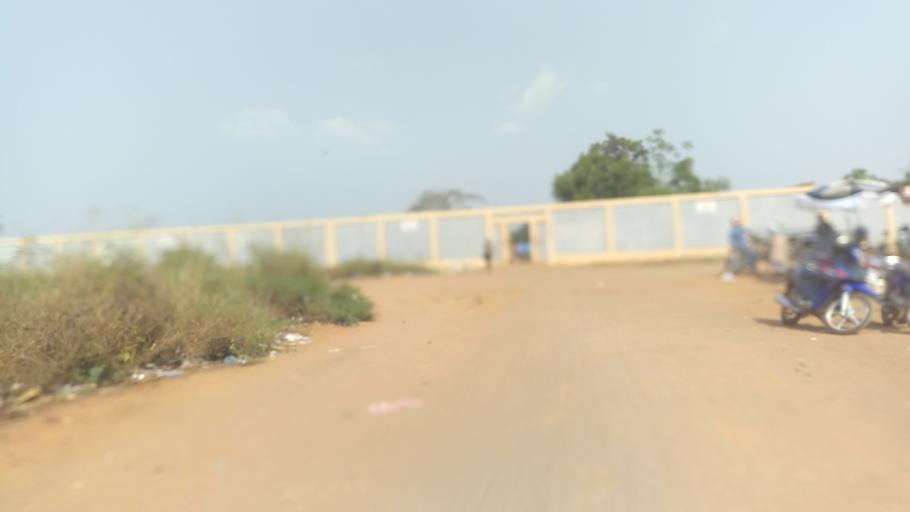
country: TG
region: Maritime
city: Lome
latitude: 6.1701
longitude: 1.2099
